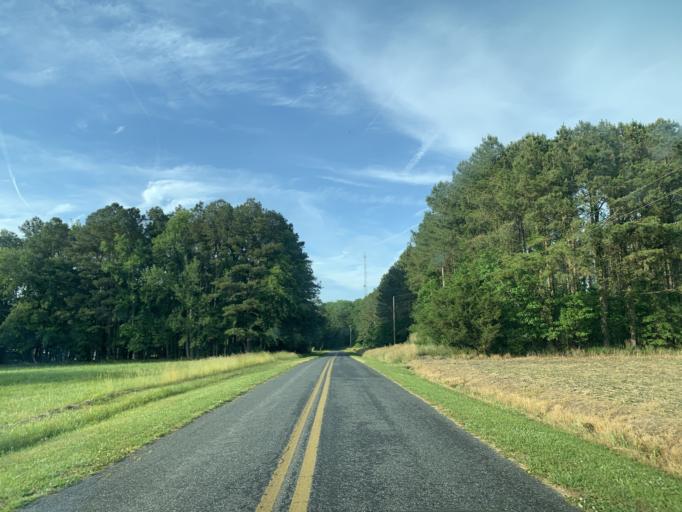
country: US
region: Maryland
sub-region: Worcester County
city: Pocomoke City
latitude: 38.0841
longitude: -75.4685
